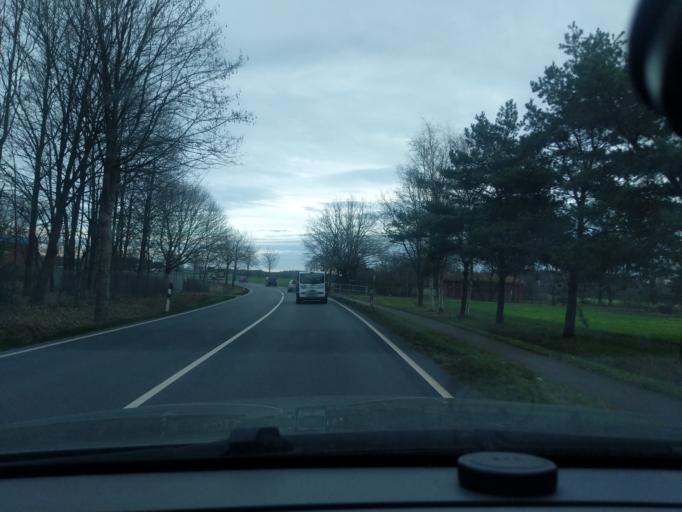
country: DE
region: Lower Saxony
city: Sauensiek
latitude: 53.3684
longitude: 9.5919
